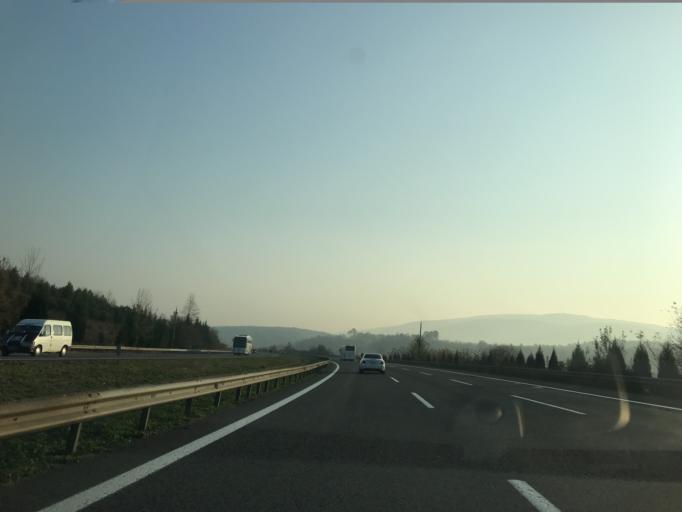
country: TR
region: Sakarya
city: Hendek
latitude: 40.7699
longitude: 30.7761
